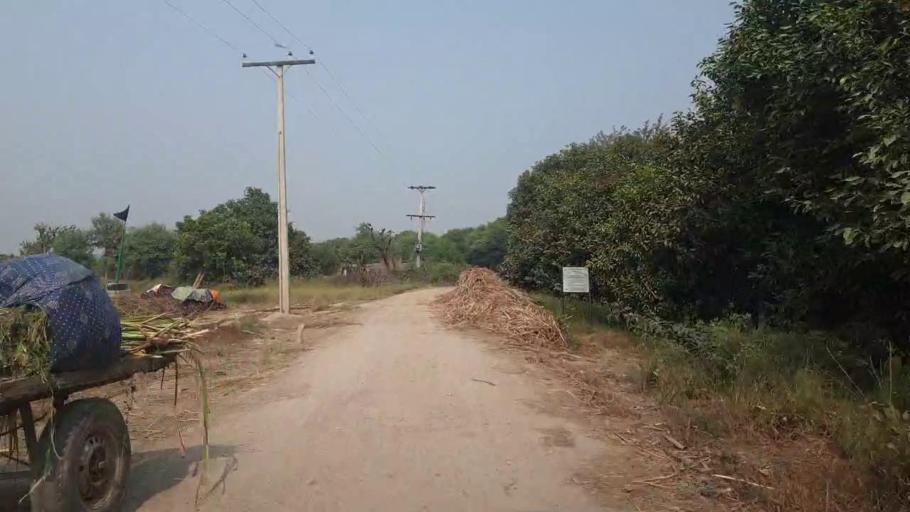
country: PK
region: Sindh
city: Tando Muhammad Khan
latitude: 25.2714
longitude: 68.5793
